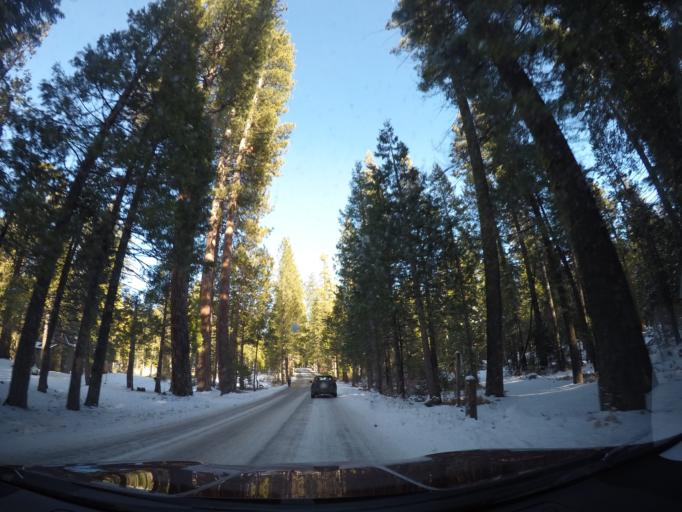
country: US
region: California
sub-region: Tuolumne County
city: Twain Harte
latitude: 38.1897
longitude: -119.9998
